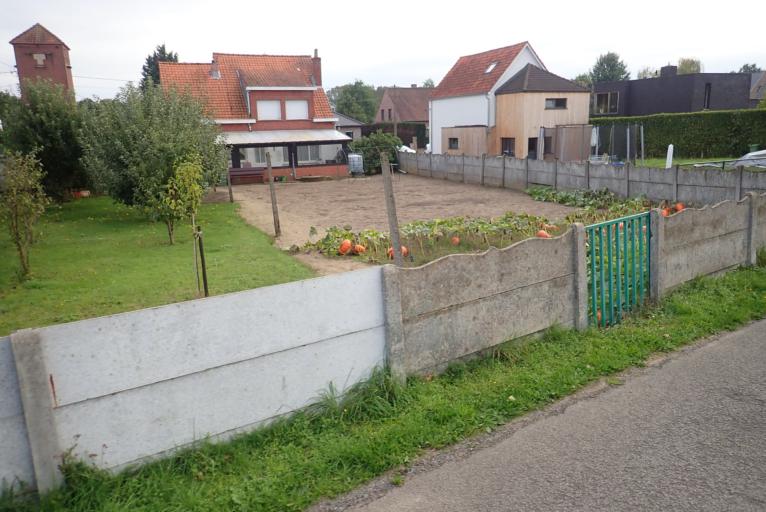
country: BE
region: Flanders
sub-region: Provincie Antwerpen
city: Grobbendonk
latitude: 51.1894
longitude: 4.7174
